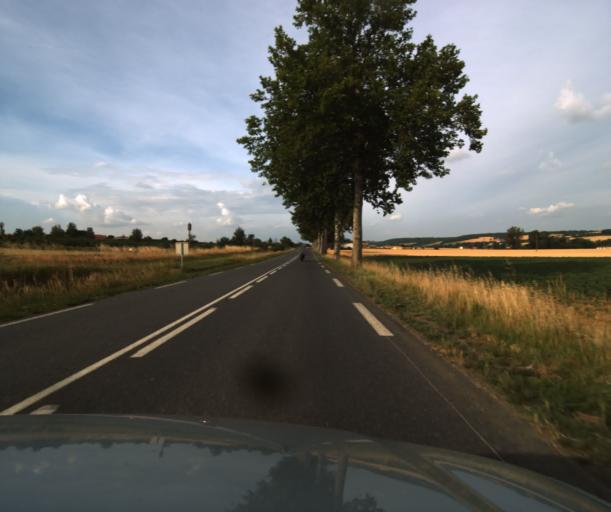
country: FR
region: Midi-Pyrenees
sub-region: Departement du Tarn-et-Garonne
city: Beaumont-de-Lomagne
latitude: 43.9240
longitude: 1.0694
